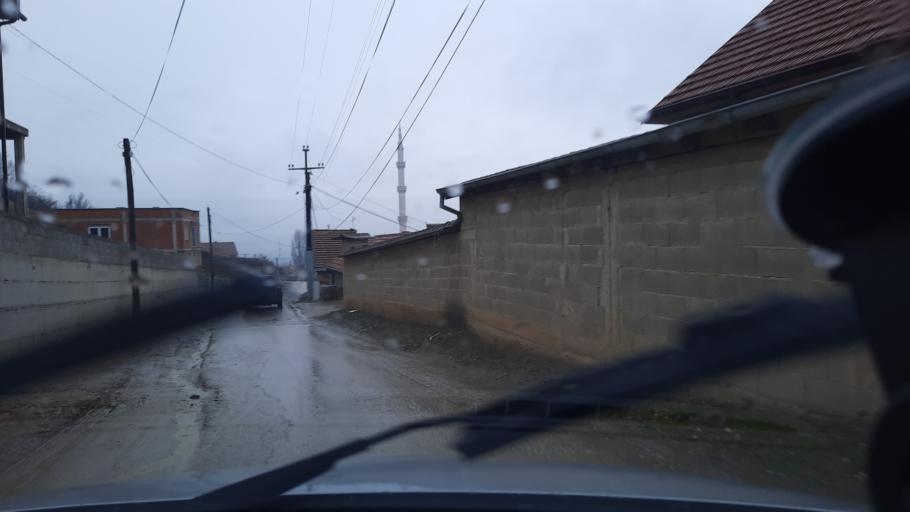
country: MK
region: Opstina Lipkovo
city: Otlja
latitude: 42.1452
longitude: 21.5813
